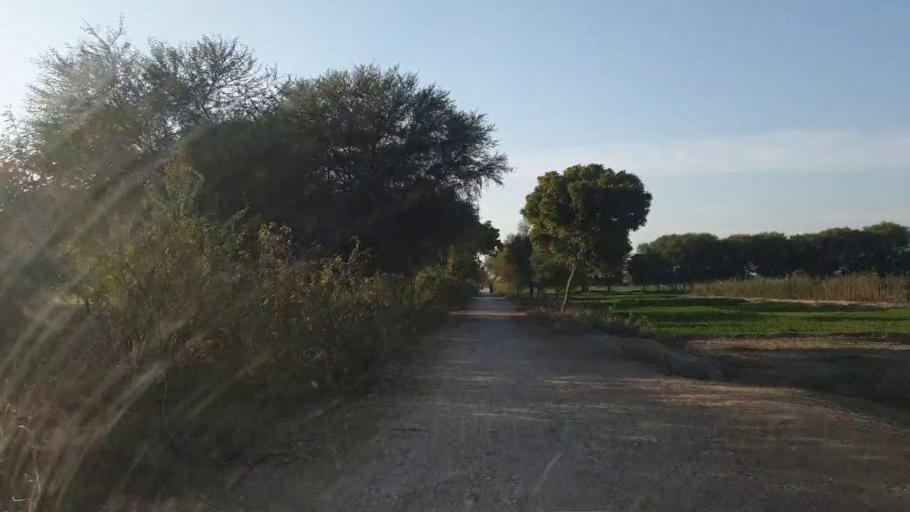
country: PK
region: Sindh
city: Chambar
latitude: 25.2812
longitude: 68.8043
